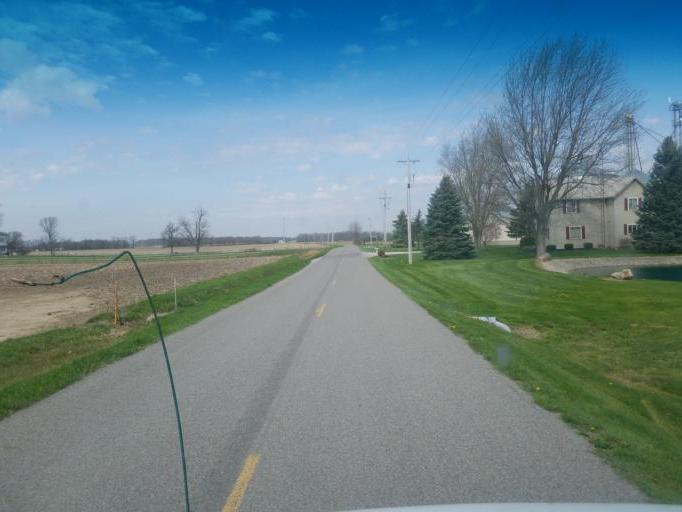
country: US
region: Ohio
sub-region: Logan County
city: Northwood
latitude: 40.4946
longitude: -83.6076
